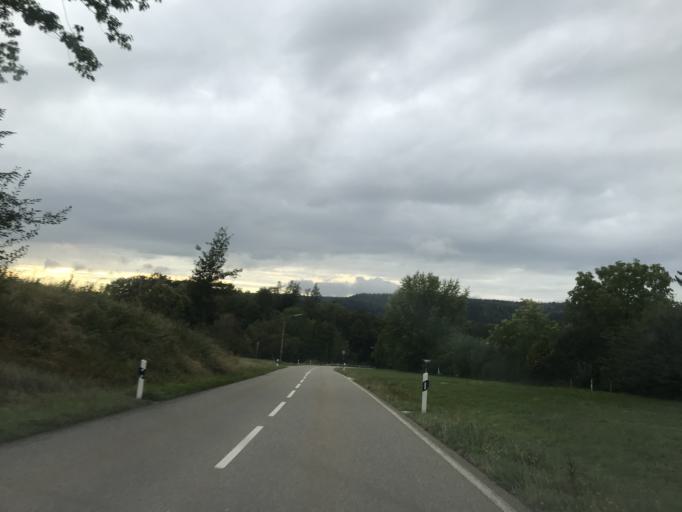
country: DE
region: Baden-Wuerttemberg
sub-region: Freiburg Region
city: Schopfheim
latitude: 47.6424
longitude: 7.8338
